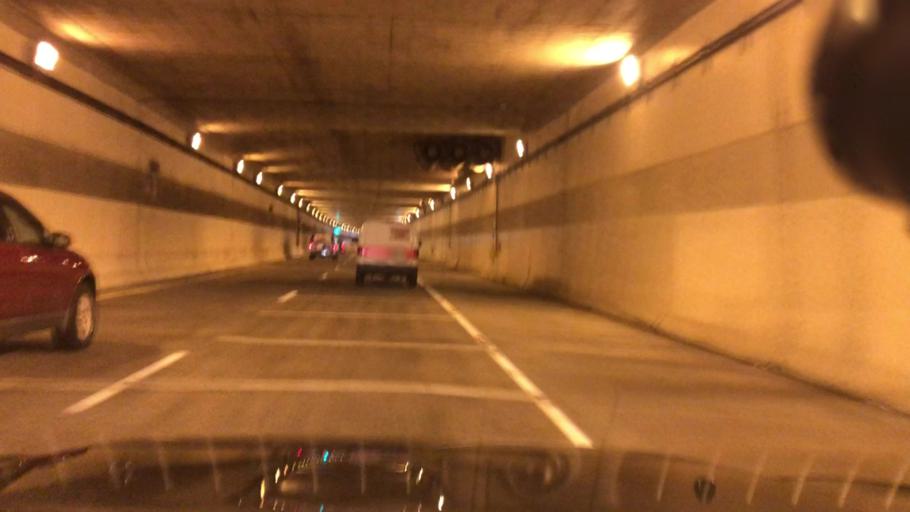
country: US
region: New Jersey
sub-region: Mercer County
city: Trenton
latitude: 40.1968
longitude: -74.7576
